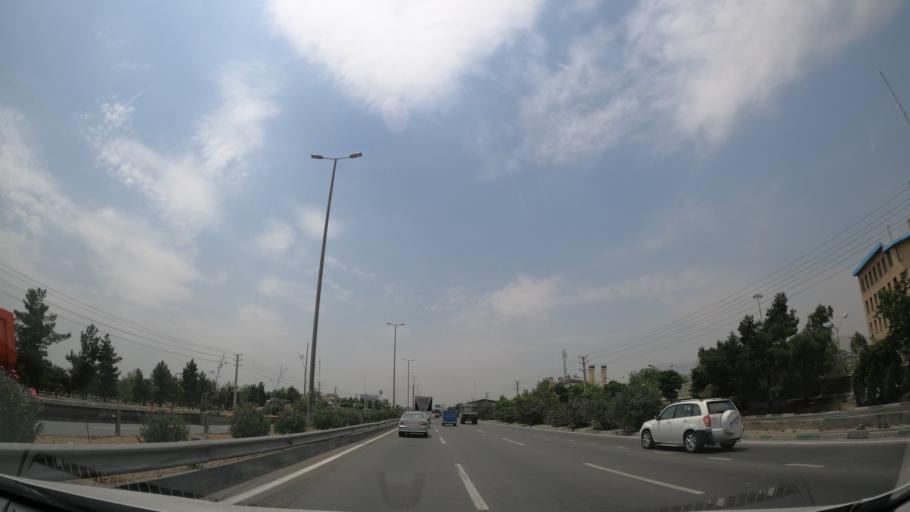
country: IR
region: Tehran
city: Shahr-e Qods
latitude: 35.7055
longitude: 51.1764
